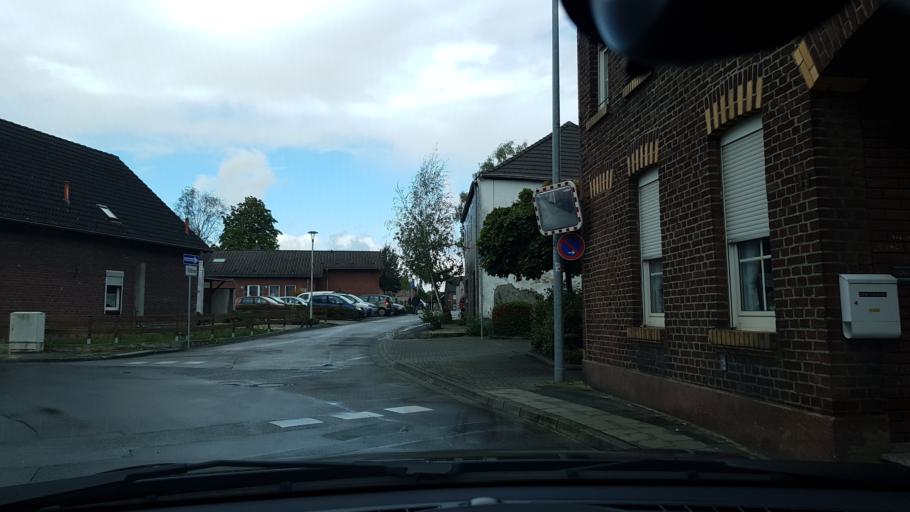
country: DE
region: North Rhine-Westphalia
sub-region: Regierungsbezirk Koln
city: Wassenberg
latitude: 51.0863
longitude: 6.1504
